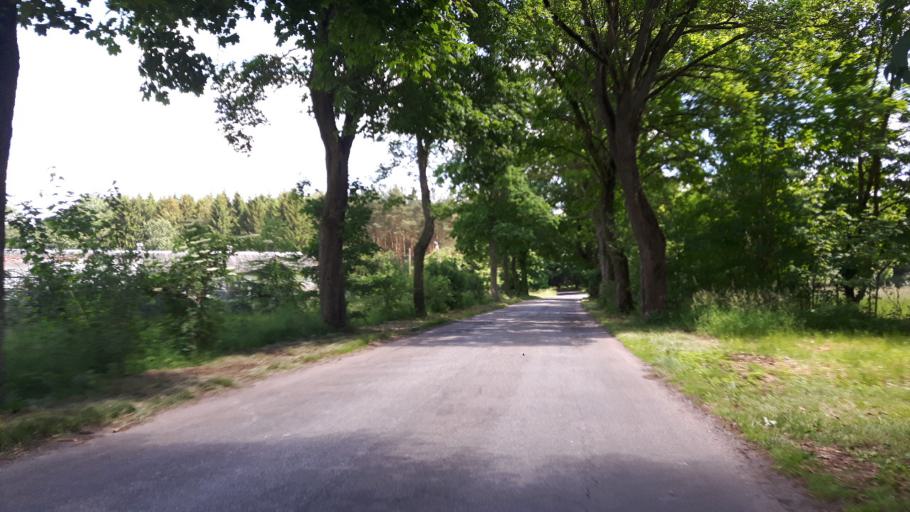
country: PL
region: West Pomeranian Voivodeship
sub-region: Powiat goleniowski
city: Osina
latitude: 53.6779
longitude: 15.0143
